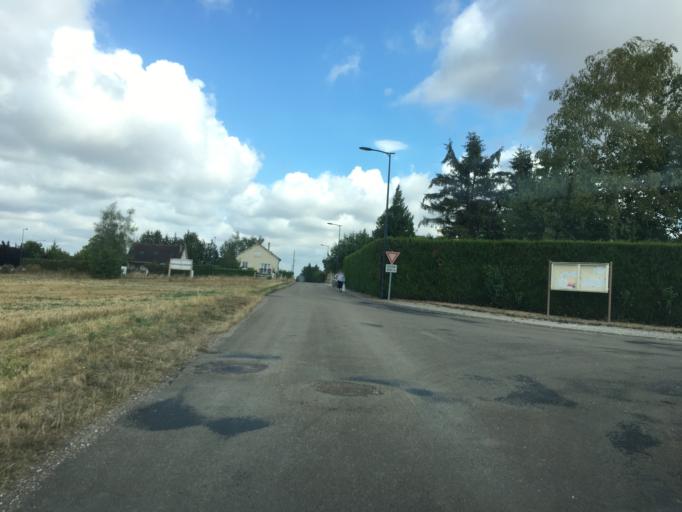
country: FR
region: Bourgogne
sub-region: Departement de l'Yonne
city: Aillant-sur-Tholon
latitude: 47.8744
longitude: 3.3555
